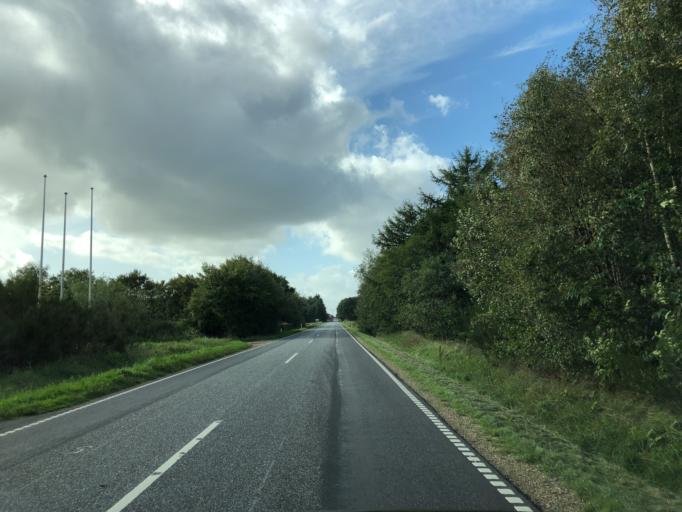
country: DK
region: Central Jutland
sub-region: Holstebro Kommune
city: Holstebro
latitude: 56.3697
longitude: 8.5629
